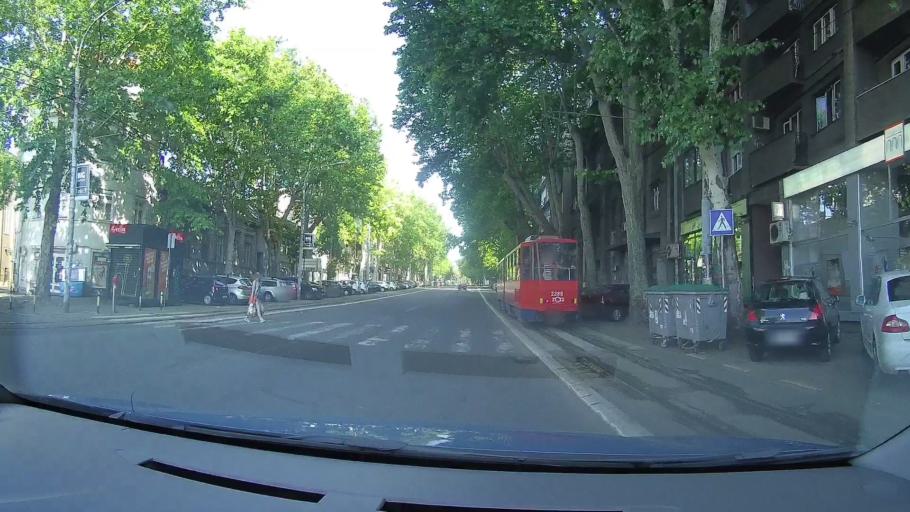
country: RS
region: Central Serbia
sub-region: Belgrade
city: Stari Grad
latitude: 44.8181
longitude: 20.4673
